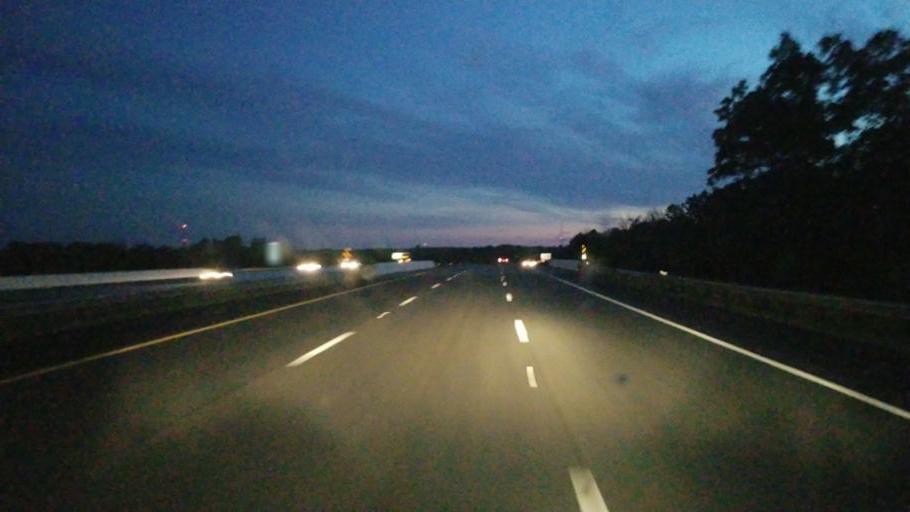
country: US
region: Ohio
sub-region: Medina County
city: Westfield Center
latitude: 41.0014
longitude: -81.9665
